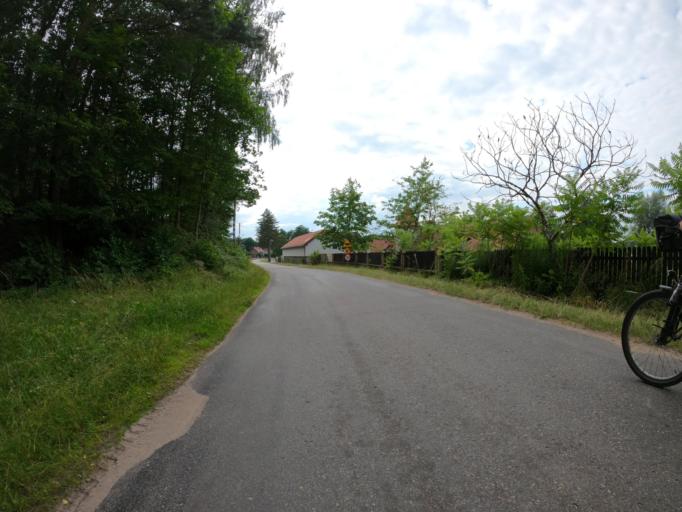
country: PL
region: West Pomeranian Voivodeship
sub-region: Powiat szczecinecki
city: Borne Sulinowo
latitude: 53.6298
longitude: 16.5639
